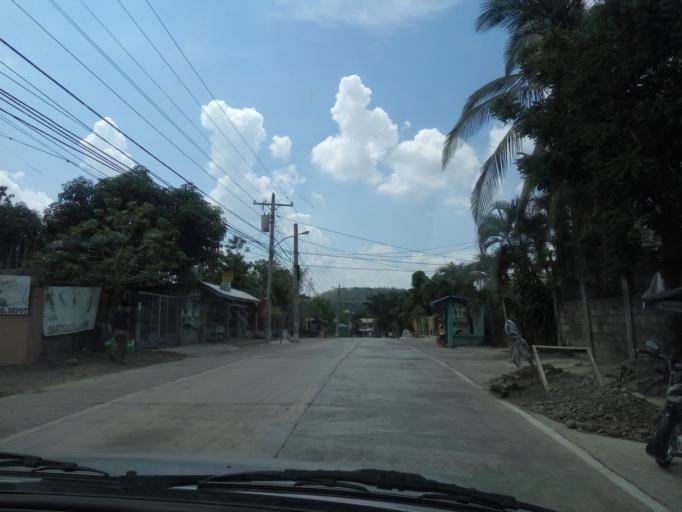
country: PH
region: Central Luzon
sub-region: Province of Nueva Ecija
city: Rizal
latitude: 15.7118
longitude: 121.1013
